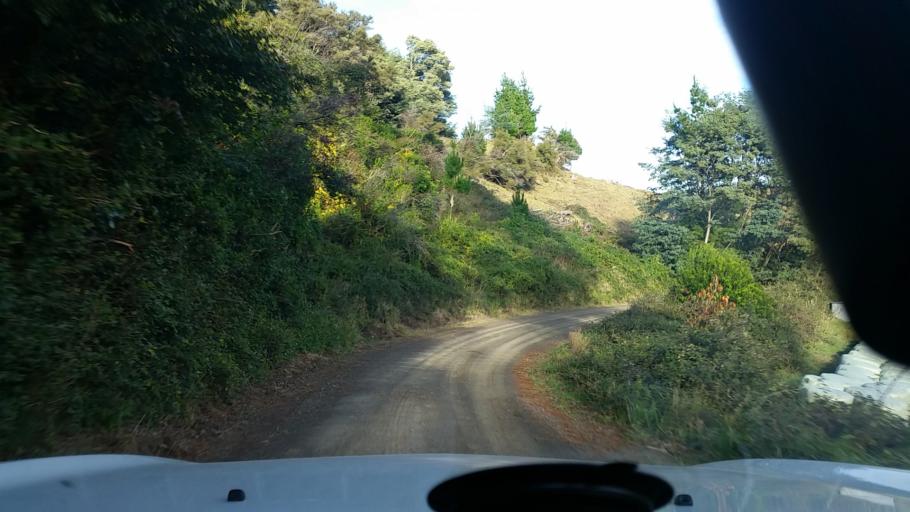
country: NZ
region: Hawke's Bay
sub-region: Napier City
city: Napier
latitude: -39.2424
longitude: 176.8137
